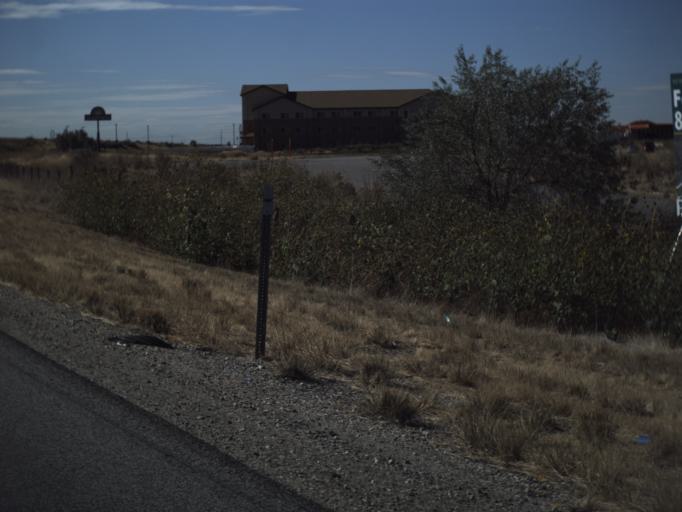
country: US
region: Utah
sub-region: Box Elder County
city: Perry
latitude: 41.4890
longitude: -112.0534
